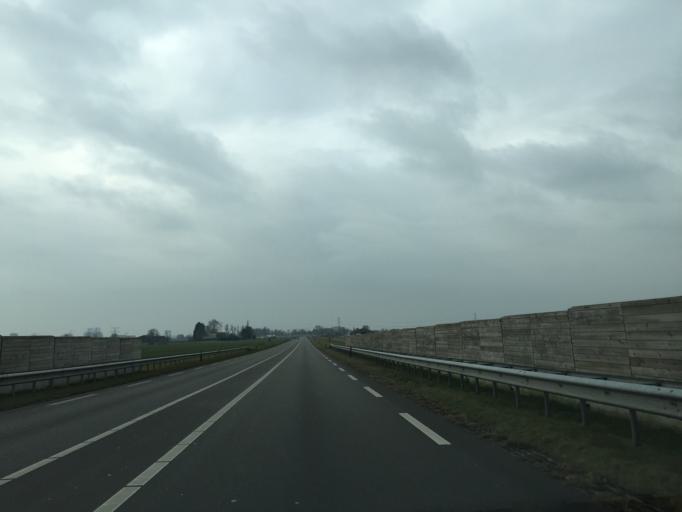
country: NL
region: South Holland
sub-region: Gemeente Waddinxveen
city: Groenswaard
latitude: 52.0063
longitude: 4.6020
